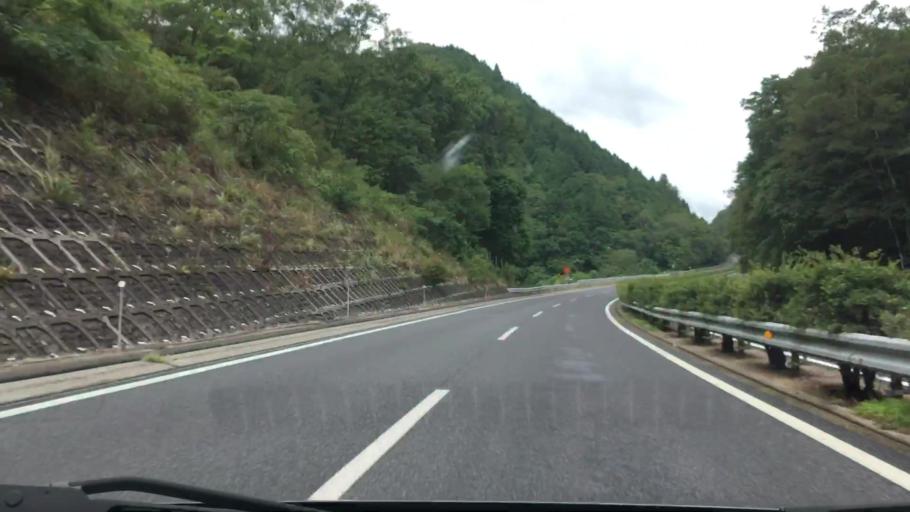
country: JP
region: Okayama
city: Tsuyama
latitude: 35.0197
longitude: 134.2067
